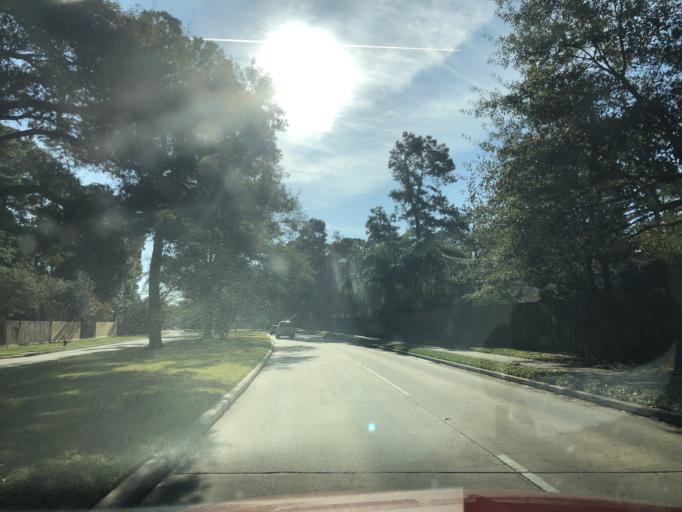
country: US
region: Texas
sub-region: Harris County
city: Tomball
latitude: 30.0186
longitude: -95.5451
